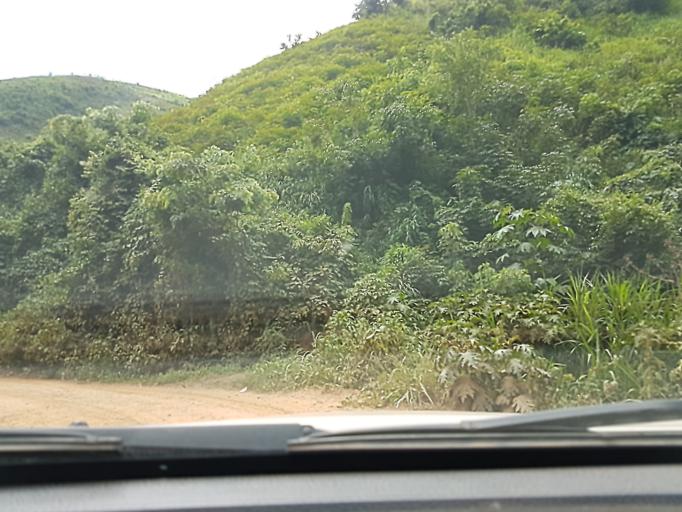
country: RW
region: Western Province
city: Cyangugu
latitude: -2.7084
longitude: 28.9429
